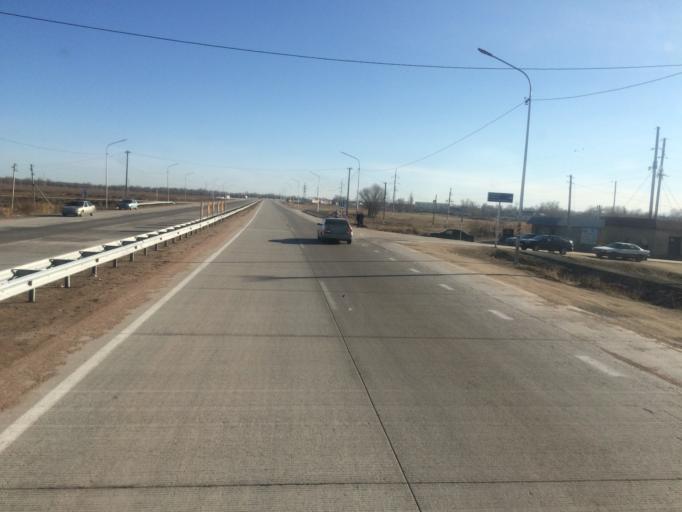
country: KG
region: Talas
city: Ivanovo-Alekseyevka
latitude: 42.9941
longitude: 72.0876
